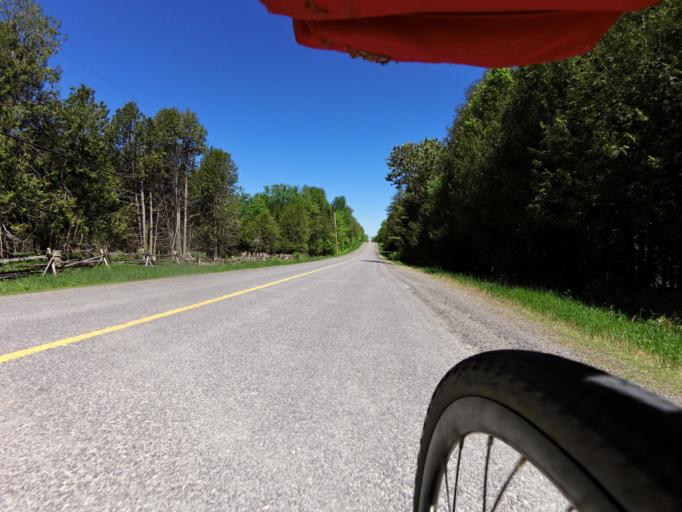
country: CA
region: Ontario
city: Carleton Place
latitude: 45.1650
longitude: -76.4244
